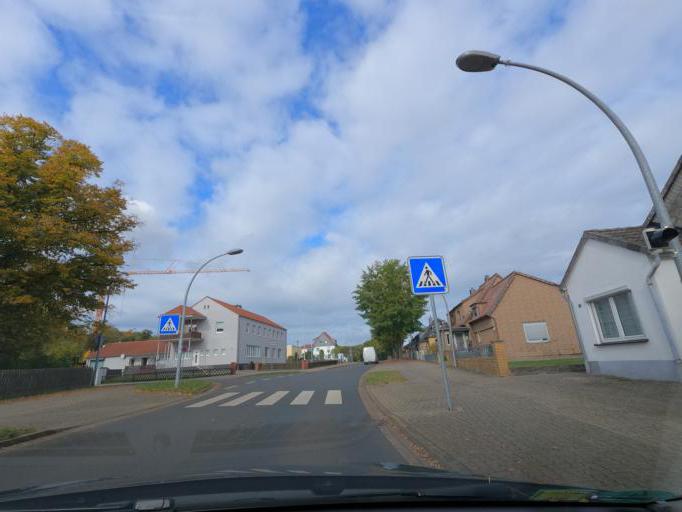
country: DE
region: Lower Saxony
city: Leiferde
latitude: 52.1921
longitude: 10.4783
